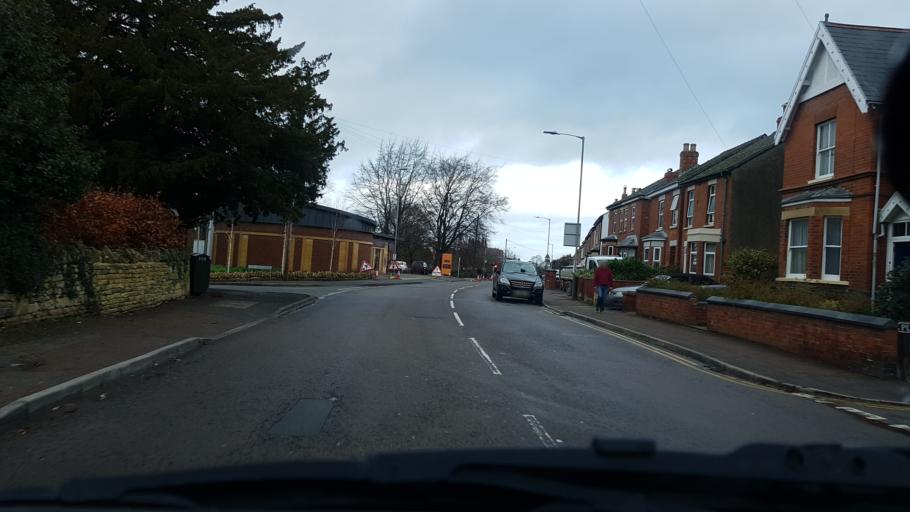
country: GB
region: England
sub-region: Gloucestershire
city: Charlton Kings
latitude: 51.8803
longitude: -2.0549
